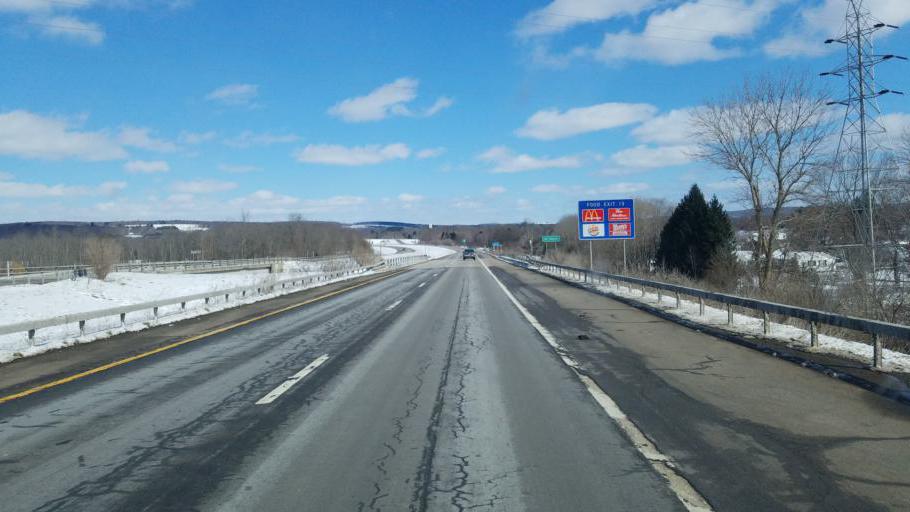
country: US
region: New York
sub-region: Chautauqua County
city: Falconer
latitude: 42.1257
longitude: -79.2040
